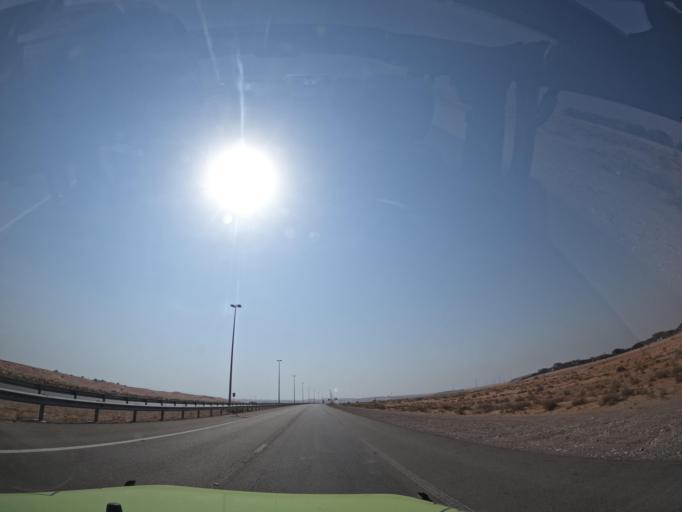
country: OM
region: Al Buraimi
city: Al Buraymi
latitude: 24.3993
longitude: 55.7157
